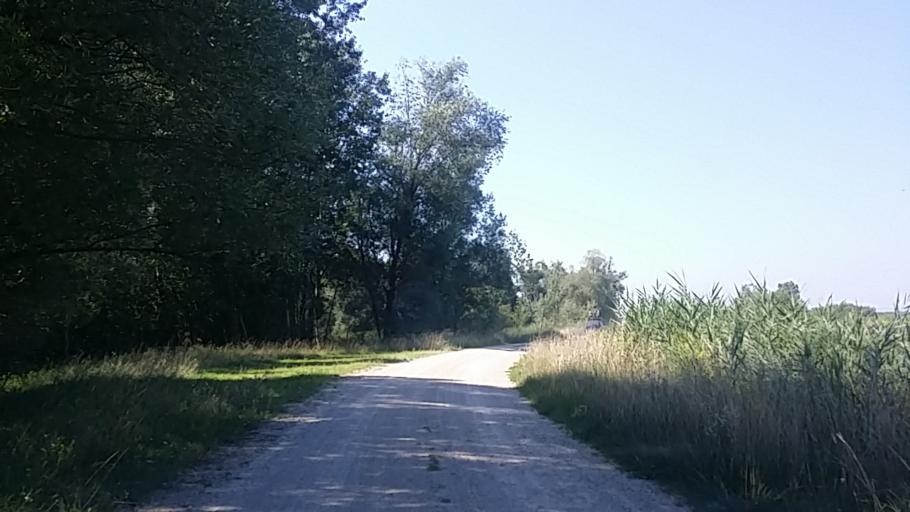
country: HU
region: Zala
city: Sarmellek
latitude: 46.6903
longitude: 17.2380
